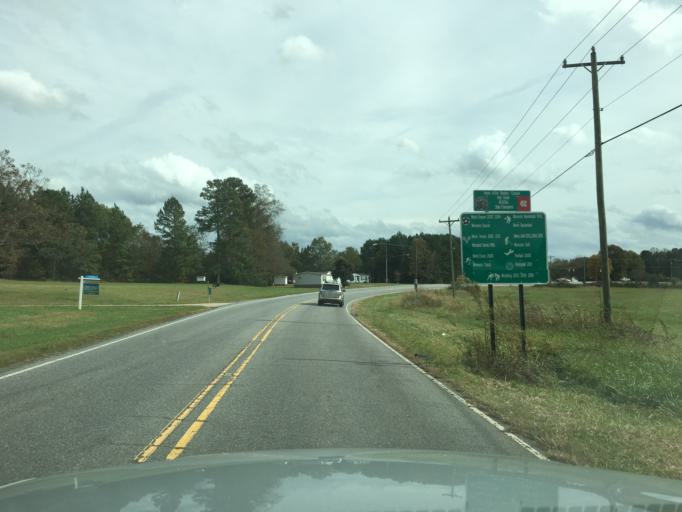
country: US
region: North Carolina
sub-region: Catawba County
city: Newton
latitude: 35.6593
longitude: -81.2691
